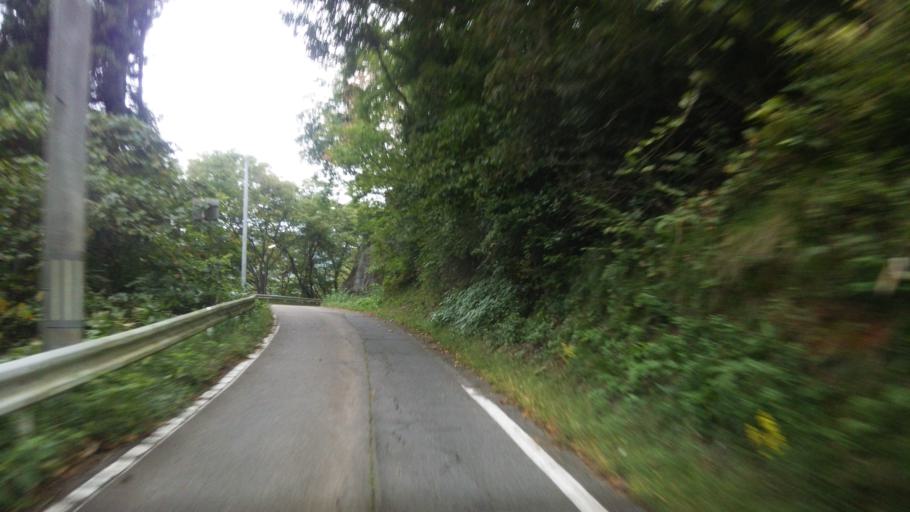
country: JP
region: Fukushima
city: Inawashiro
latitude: 37.3716
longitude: 139.9230
